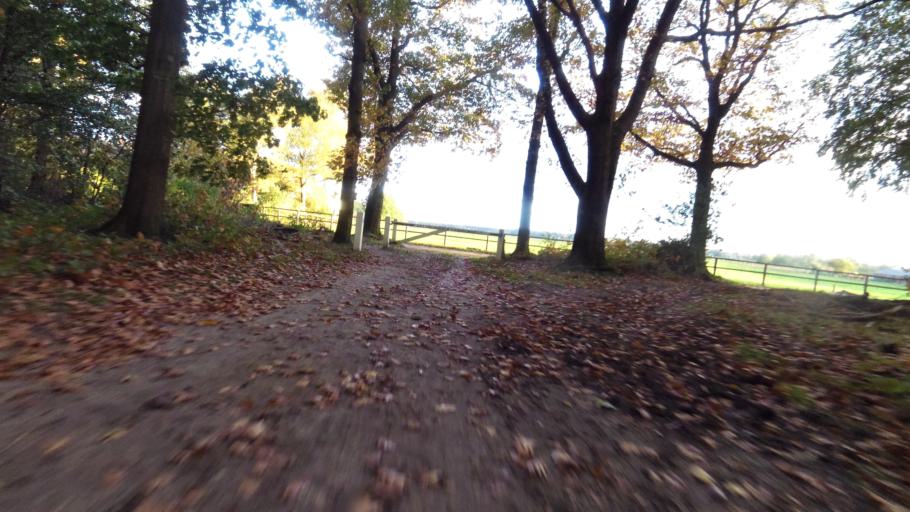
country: NL
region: Gelderland
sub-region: Gemeente Ede
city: Wekerom
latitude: 52.0867
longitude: 5.6738
